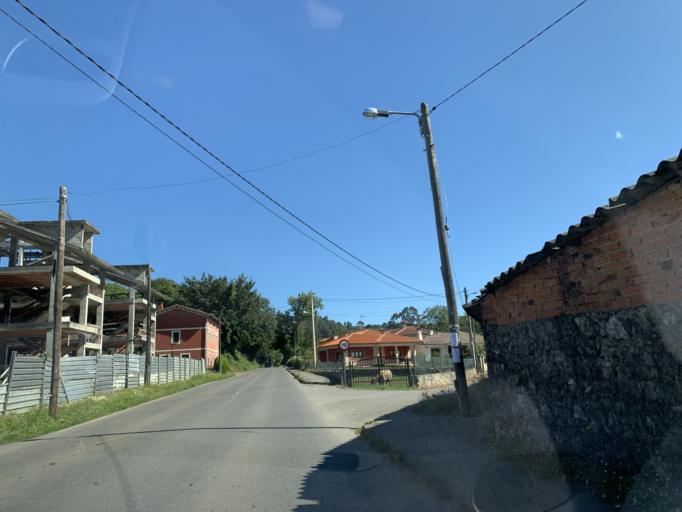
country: ES
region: Asturias
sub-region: Province of Asturias
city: Llanes
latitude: 43.4271
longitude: -4.8627
